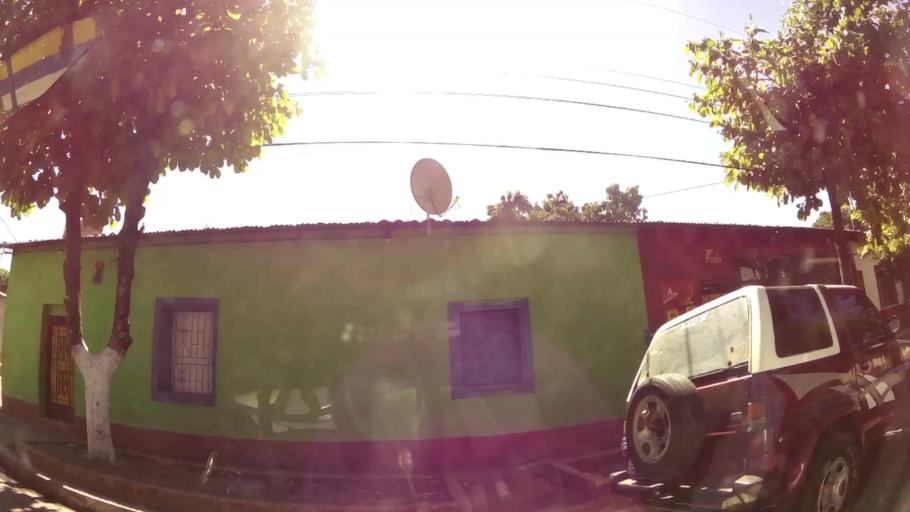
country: SV
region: Santa Ana
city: Chalchuapa
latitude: 13.9748
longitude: -89.7062
